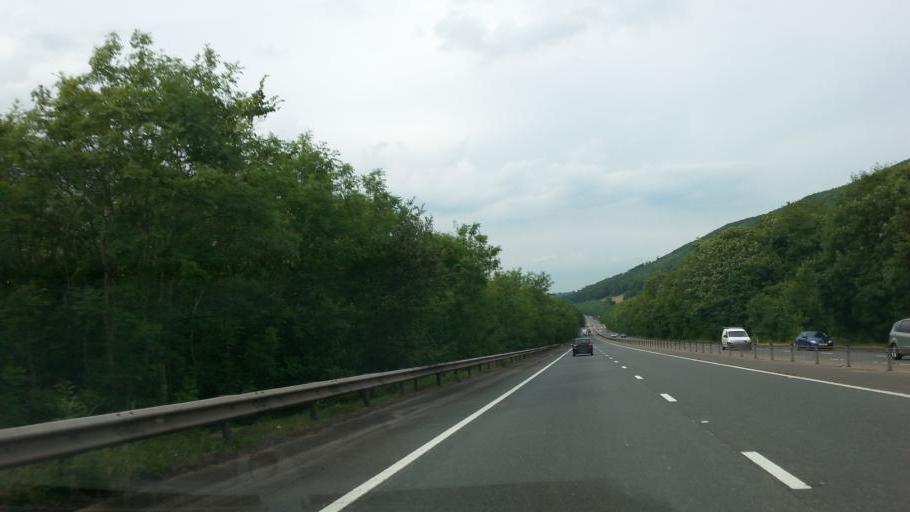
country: GB
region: Wales
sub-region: Newport
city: Langstone
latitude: 51.6267
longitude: -2.8997
